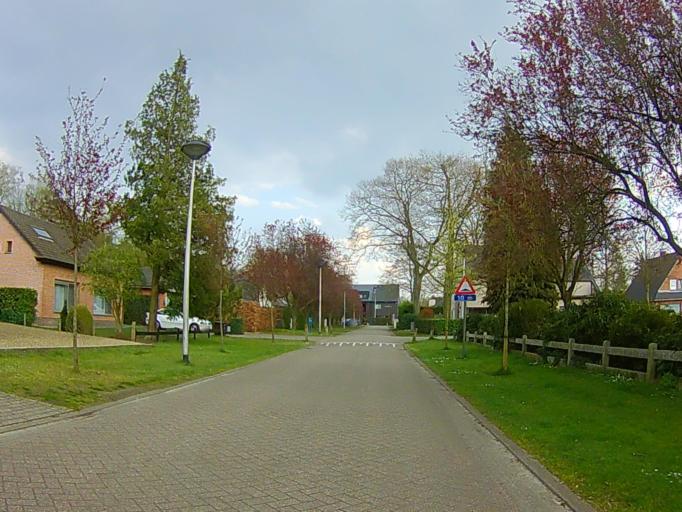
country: BE
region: Flanders
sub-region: Provincie Antwerpen
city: Kapellen
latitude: 51.3256
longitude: 4.4424
